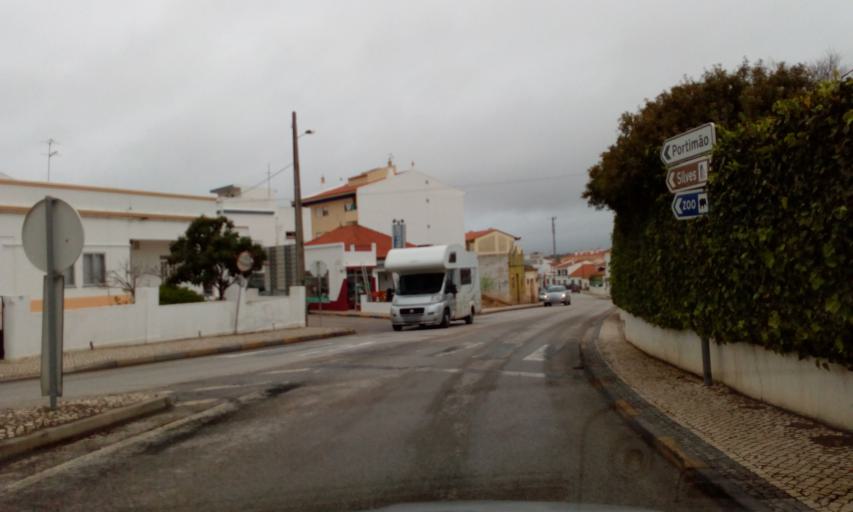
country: PT
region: Faro
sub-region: Albufeira
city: Guia
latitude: 37.1621
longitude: -8.3011
